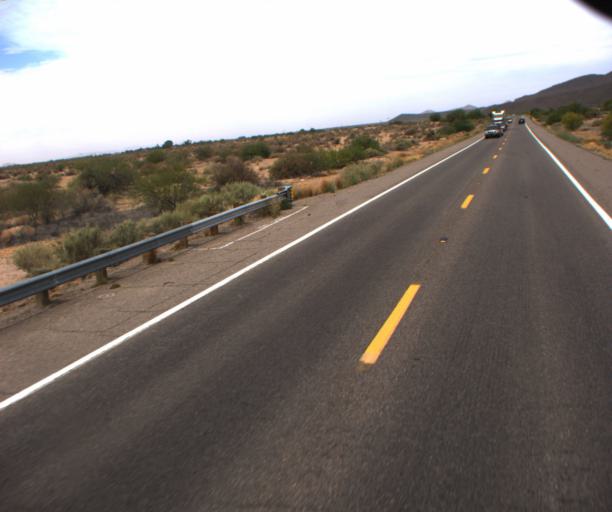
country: US
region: Arizona
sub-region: Pinal County
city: Sacaton
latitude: 33.0918
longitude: -111.7088
